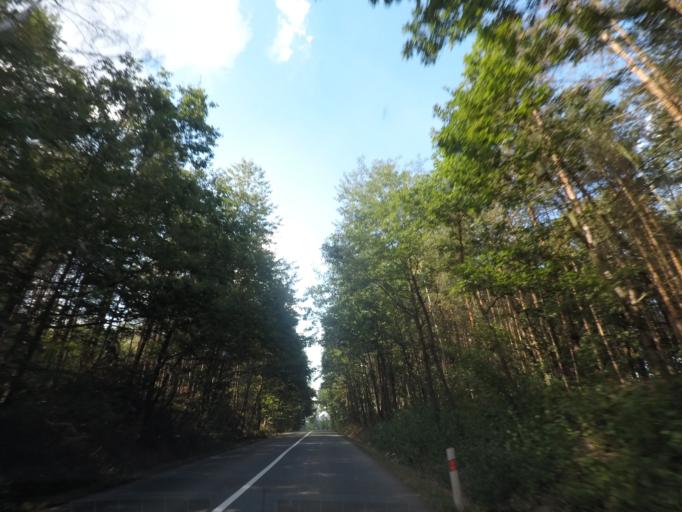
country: CZ
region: Kralovehradecky
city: Trebechovice pod Orebem
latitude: 50.2214
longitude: 15.9758
